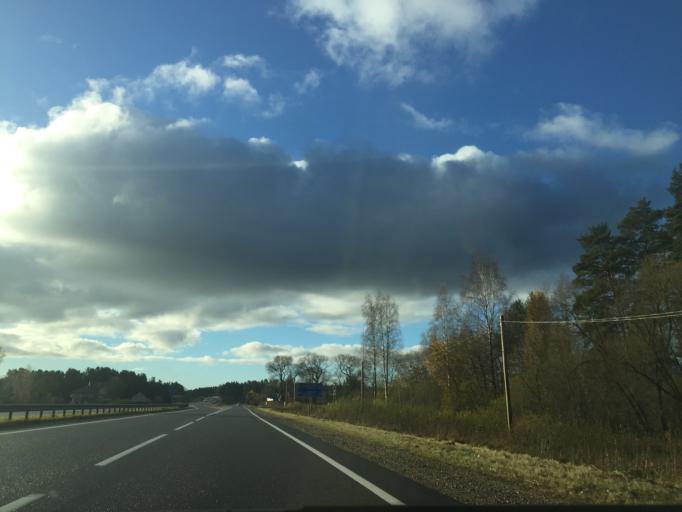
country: LV
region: Babite
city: Pinki
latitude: 56.9296
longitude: 23.9161
